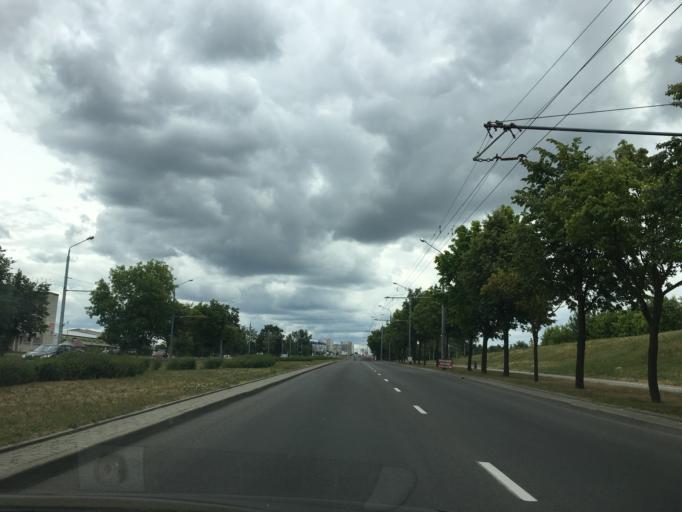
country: BY
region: Grodnenskaya
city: Hrodna
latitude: 53.6652
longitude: 23.8608
